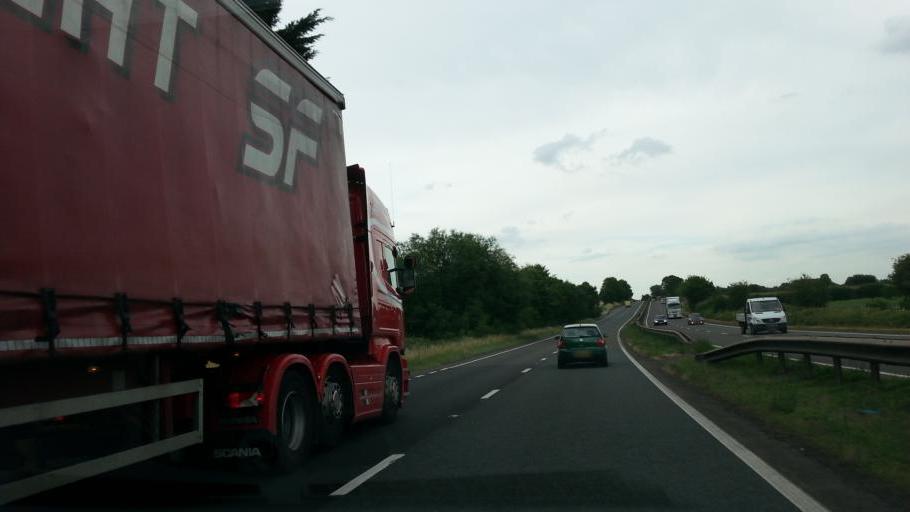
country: GB
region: England
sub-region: Herefordshire
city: Walford
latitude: 51.9121
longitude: -2.6133
